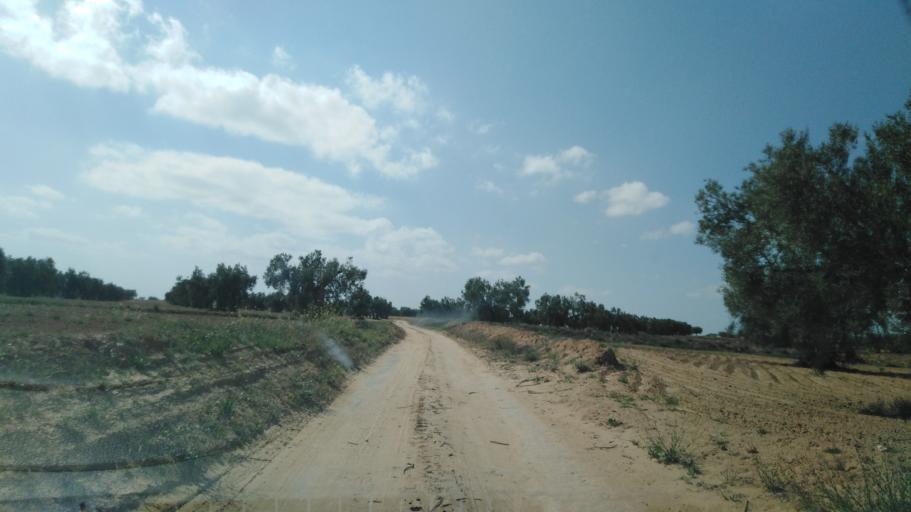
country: TN
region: Safaqis
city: Bi'r `Ali Bin Khalifah
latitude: 34.7935
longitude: 10.3974
